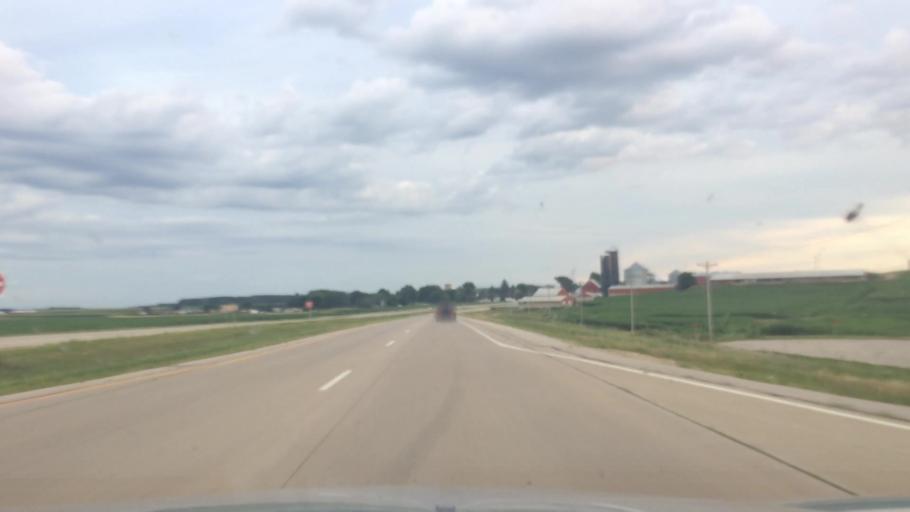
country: US
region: Wisconsin
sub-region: Dane County
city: Middleton
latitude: 43.1599
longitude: -89.5322
